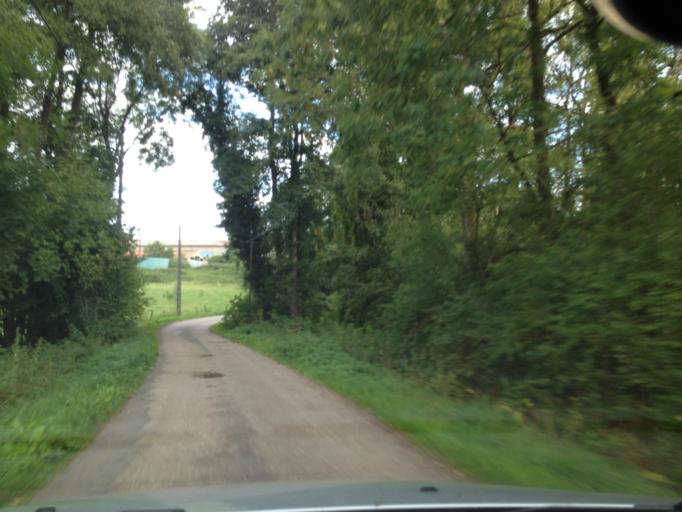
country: FR
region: Lorraine
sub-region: Departement des Vosges
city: Bains-les-Bains
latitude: 47.9804
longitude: 6.2006
